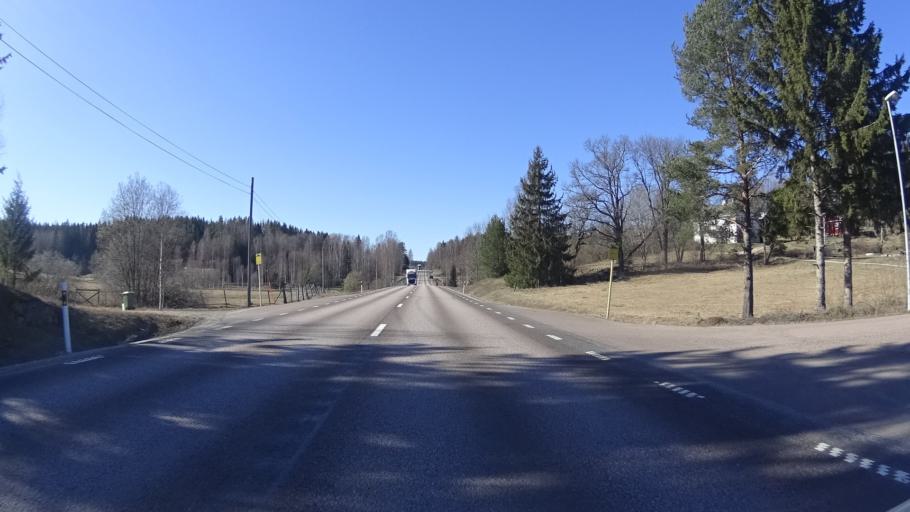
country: SE
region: Vaermland
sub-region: Sunne Kommun
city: Sunne
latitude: 59.6624
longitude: 12.9243
